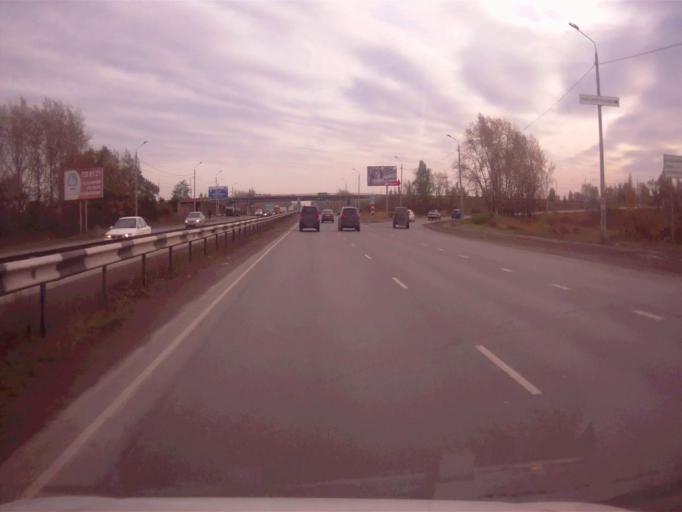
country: RU
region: Chelyabinsk
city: Novosineglazovskiy
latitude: 55.0640
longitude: 61.3980
